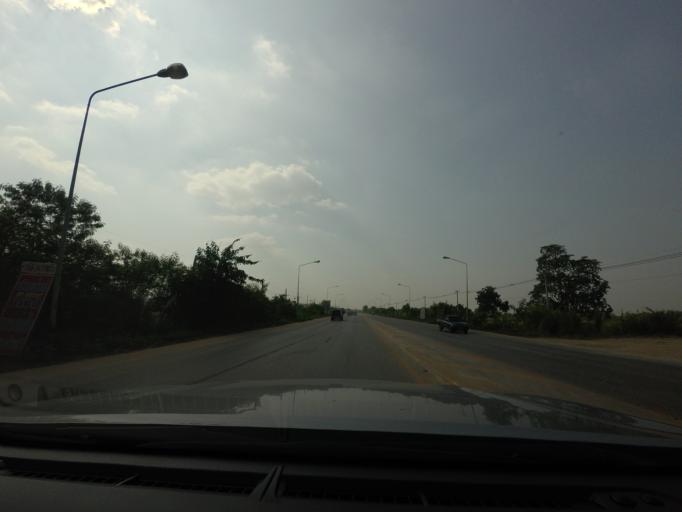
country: TH
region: Phitsanulok
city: Bang Rakam
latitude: 16.7460
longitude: 100.1084
